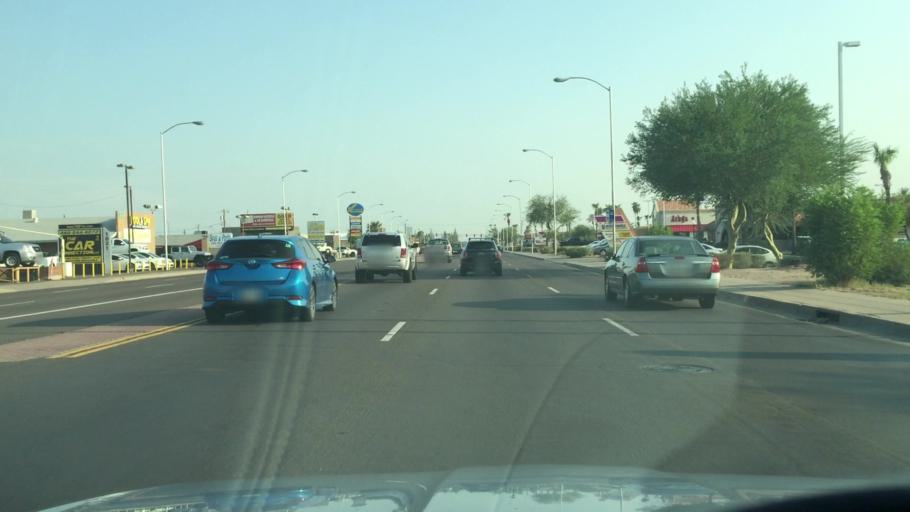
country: US
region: Arizona
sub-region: Maricopa County
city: Mesa
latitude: 33.3972
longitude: -111.8381
